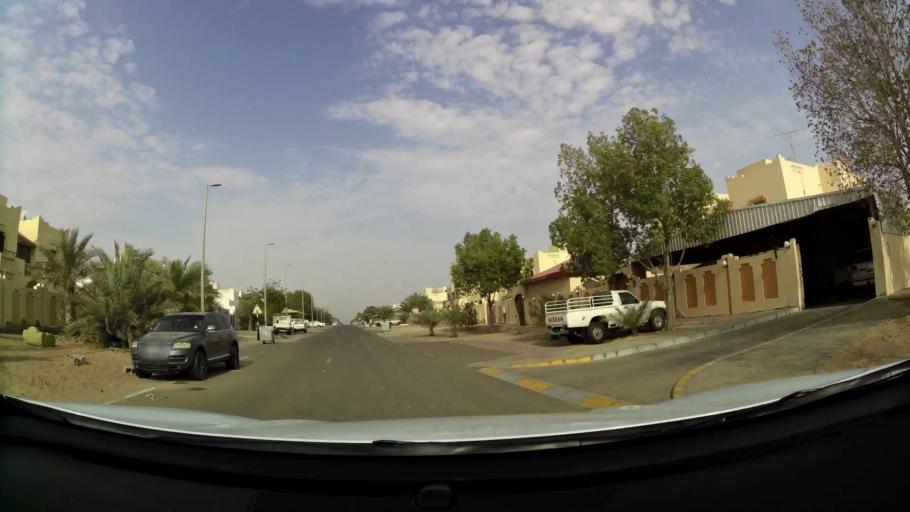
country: AE
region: Abu Dhabi
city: Abu Dhabi
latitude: 24.2380
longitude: 54.7254
